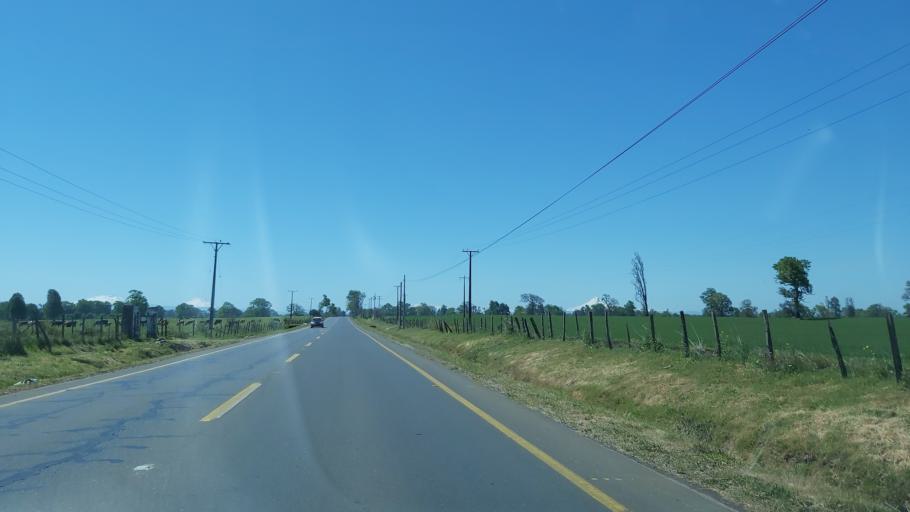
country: CL
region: Araucania
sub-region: Provincia de Malleco
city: Victoria
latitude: -38.2465
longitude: -72.3118
